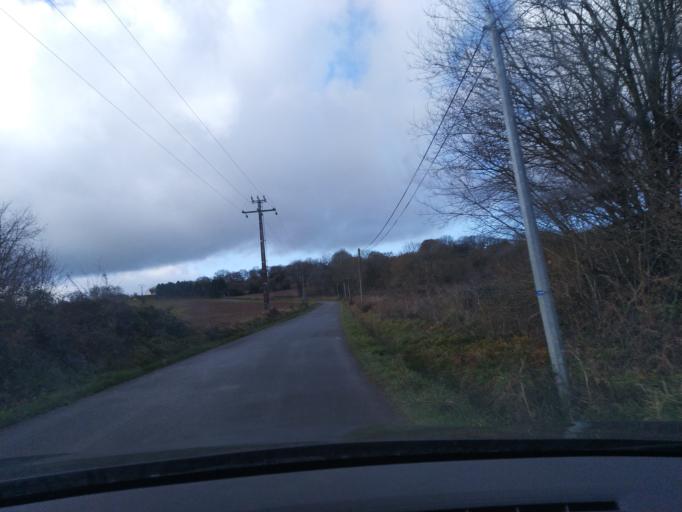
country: FR
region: Brittany
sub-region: Departement du Finistere
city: Guerlesquin
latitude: 48.4294
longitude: -3.6071
